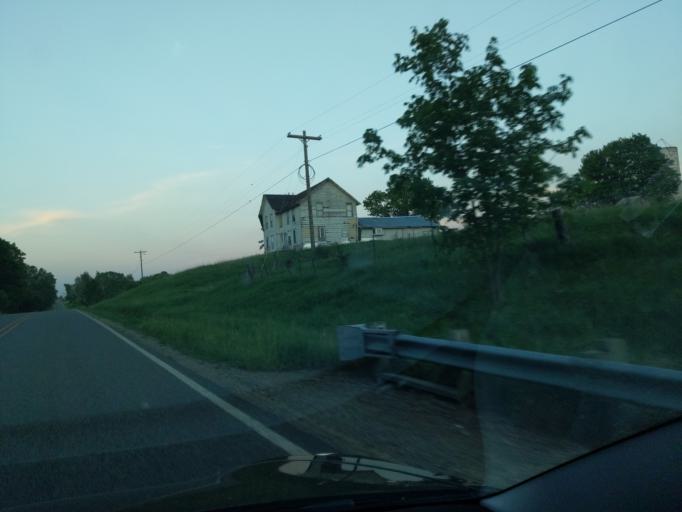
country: US
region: Michigan
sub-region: Barry County
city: Nashville
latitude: 42.5380
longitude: -85.0884
